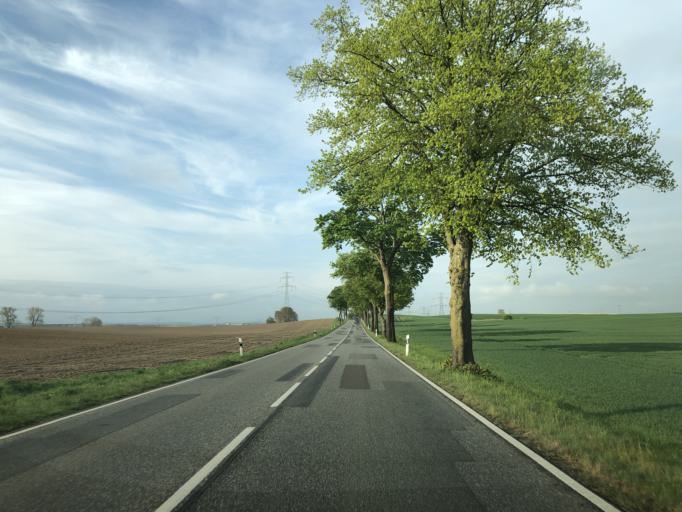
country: DE
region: Mecklenburg-Vorpommern
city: Guestrow
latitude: 53.8348
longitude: 12.2110
